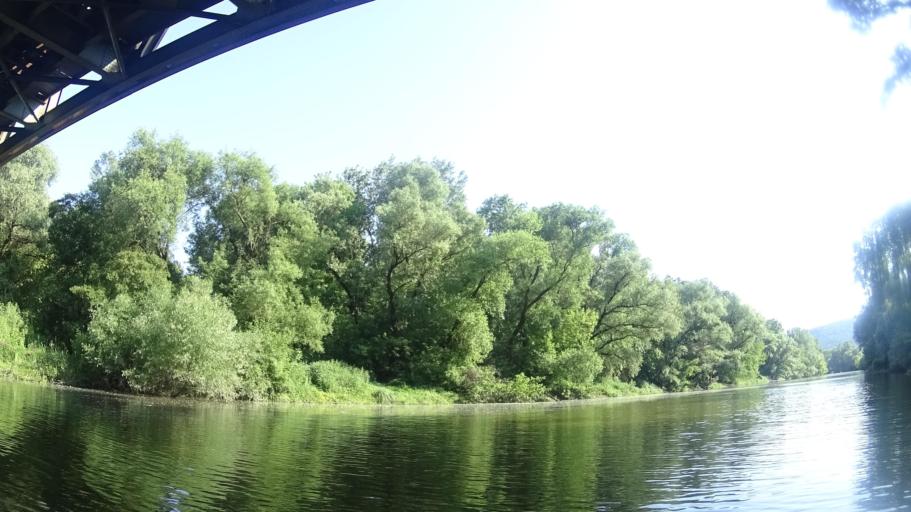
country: HU
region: Pest
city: Szob
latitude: 47.8237
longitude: 18.8527
